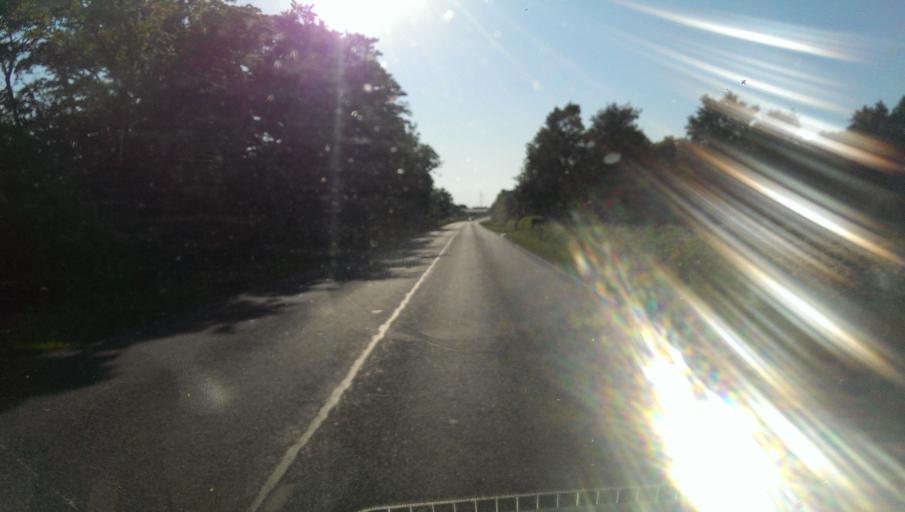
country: DK
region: South Denmark
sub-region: Esbjerg Kommune
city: Bramming
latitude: 55.5236
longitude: 8.6972
